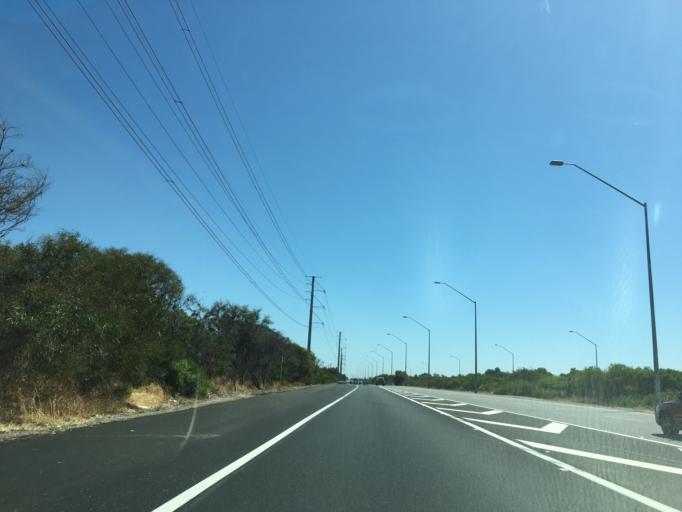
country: AU
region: Western Australia
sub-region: Canning
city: Canning Vale
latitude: -32.0591
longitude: 115.9028
